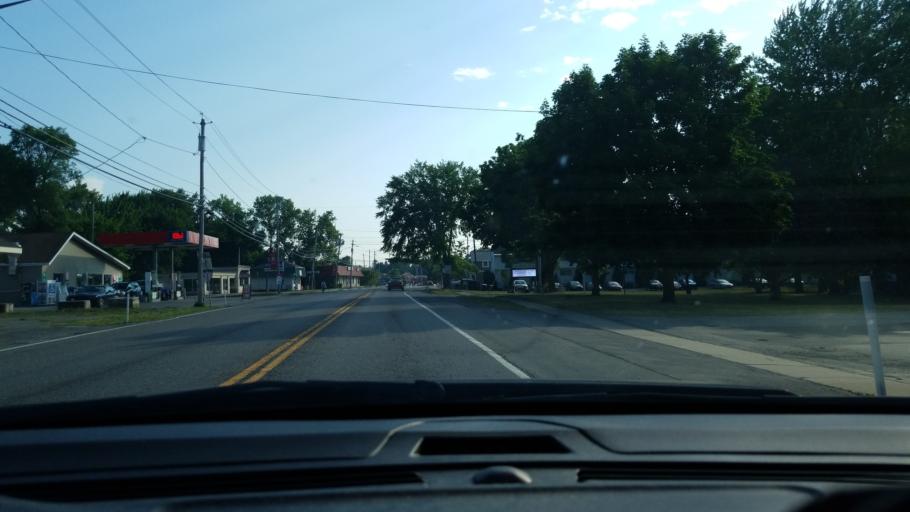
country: US
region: New York
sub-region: Onondaga County
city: North Syracuse
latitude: 43.1259
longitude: -76.1379
